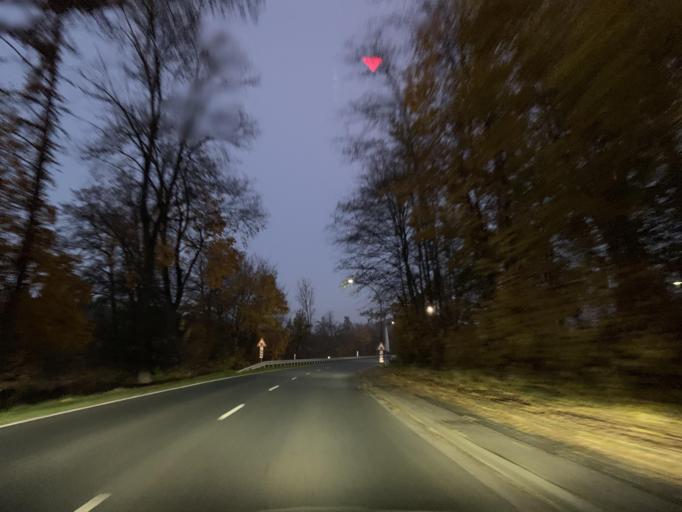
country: DE
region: Bavaria
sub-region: Upper Palatinate
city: Bodenwohr
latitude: 49.2712
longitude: 12.3092
